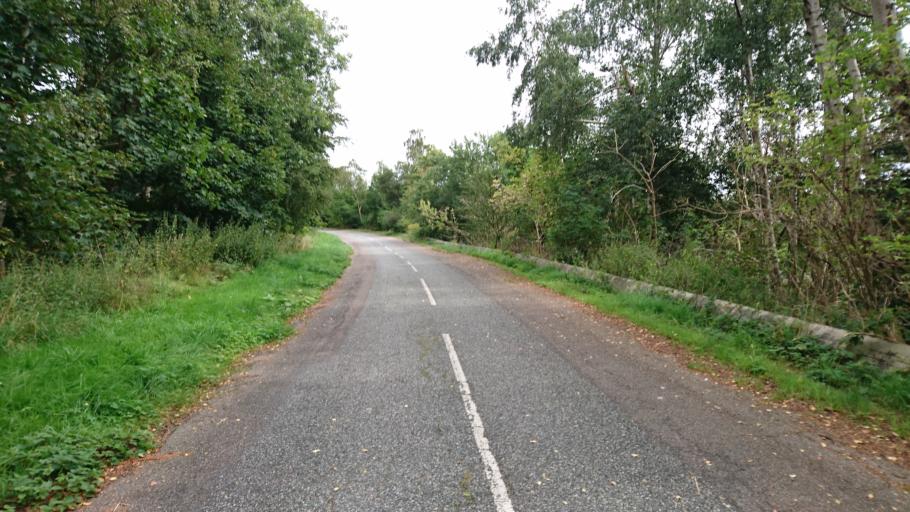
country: DK
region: Capital Region
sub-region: Ballerup Kommune
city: Malov
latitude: 55.7621
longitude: 12.3298
